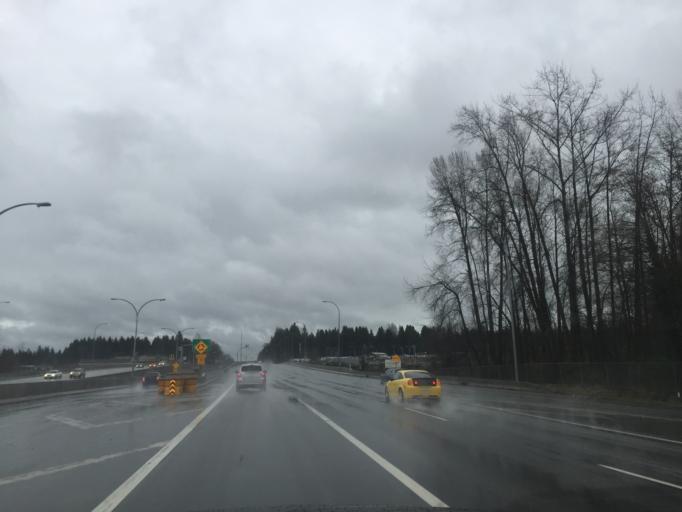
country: CA
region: British Columbia
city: Walnut Grove
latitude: 49.1627
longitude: -122.6639
